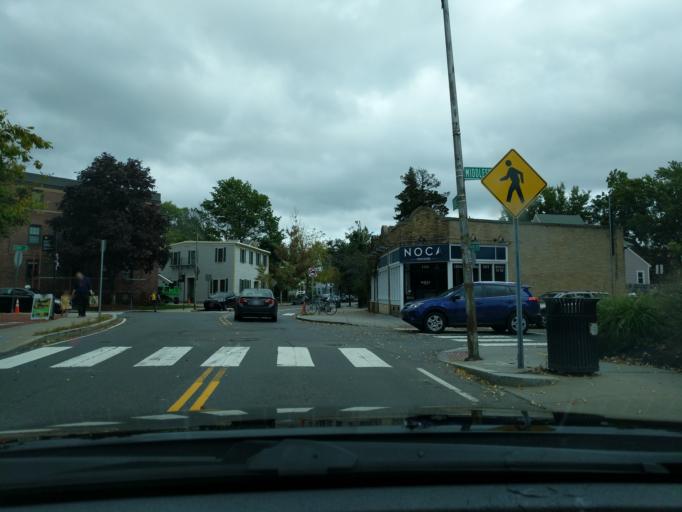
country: US
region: Massachusetts
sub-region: Middlesex County
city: Cambridge
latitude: 42.3934
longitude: -71.1312
